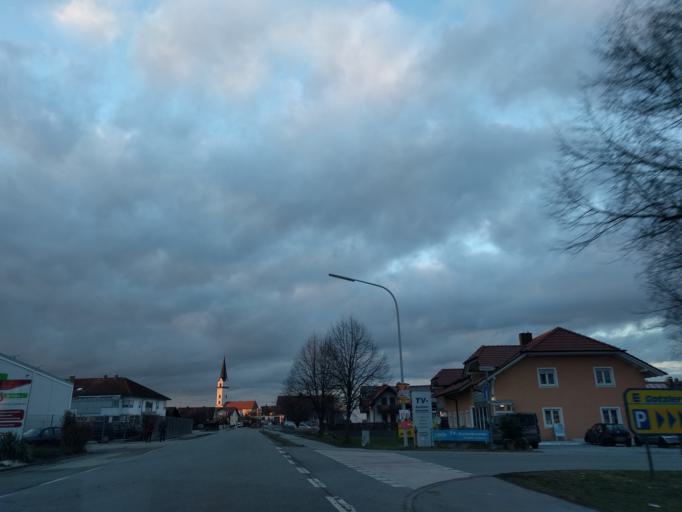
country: DE
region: Bavaria
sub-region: Lower Bavaria
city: Hofkirchen
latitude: 48.6746
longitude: 13.1212
